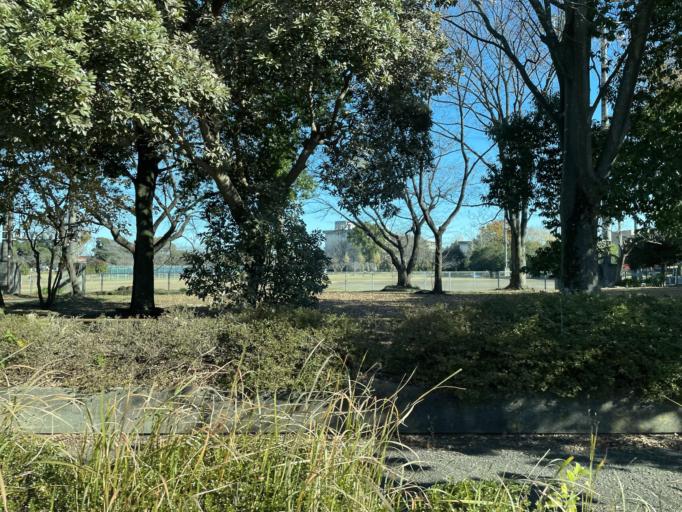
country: JP
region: Saitama
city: Kukichuo
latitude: 36.0708
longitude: 139.6955
